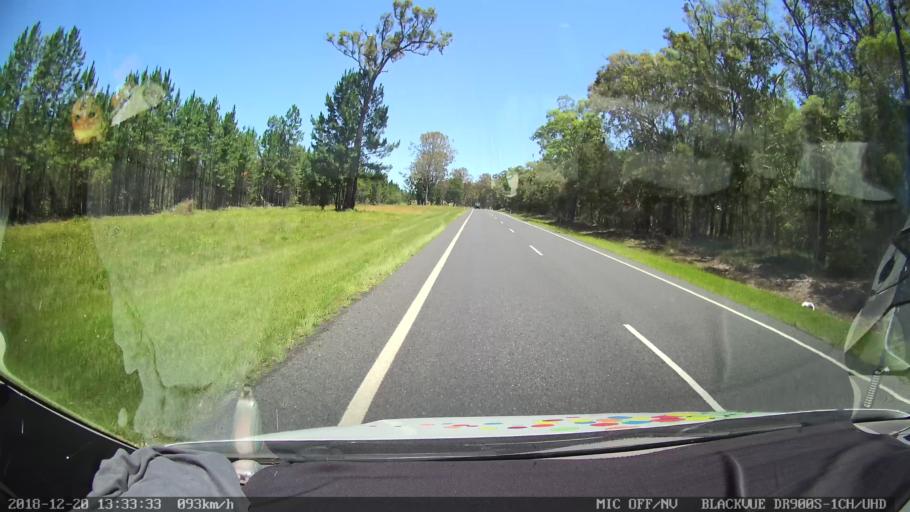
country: AU
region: New South Wales
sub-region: Clarence Valley
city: Gordon
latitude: -29.2469
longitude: 152.9861
